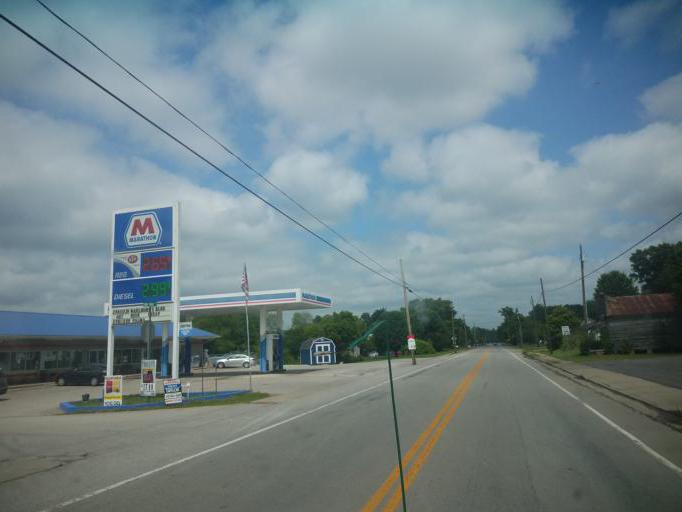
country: US
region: Kentucky
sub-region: Cumberland County
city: Burkesville
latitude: 36.8279
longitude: -85.5081
